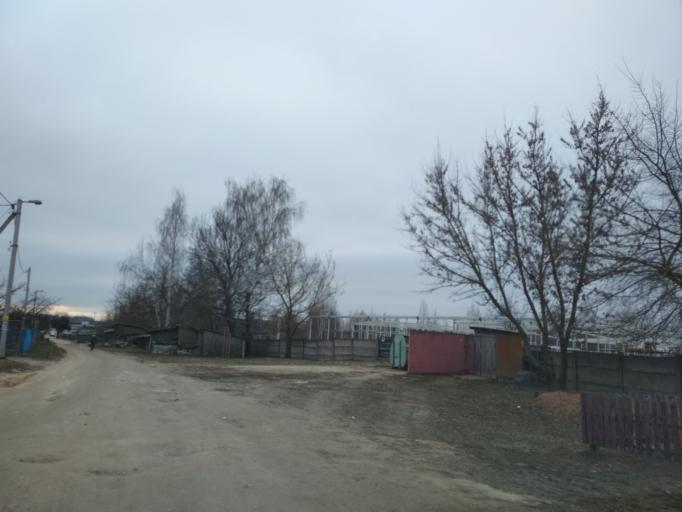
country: BY
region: Minsk
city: Mar''ina Horka
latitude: 53.5066
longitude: 28.1524
